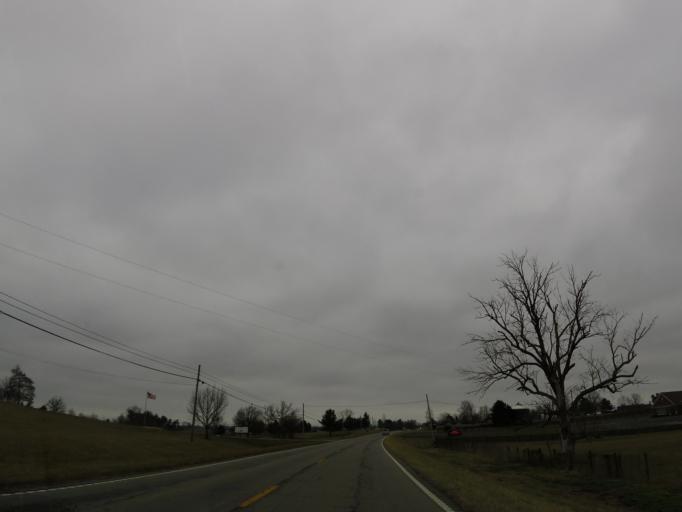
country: US
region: Kentucky
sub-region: Henry County
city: New Castle
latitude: 38.4614
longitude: -85.1648
